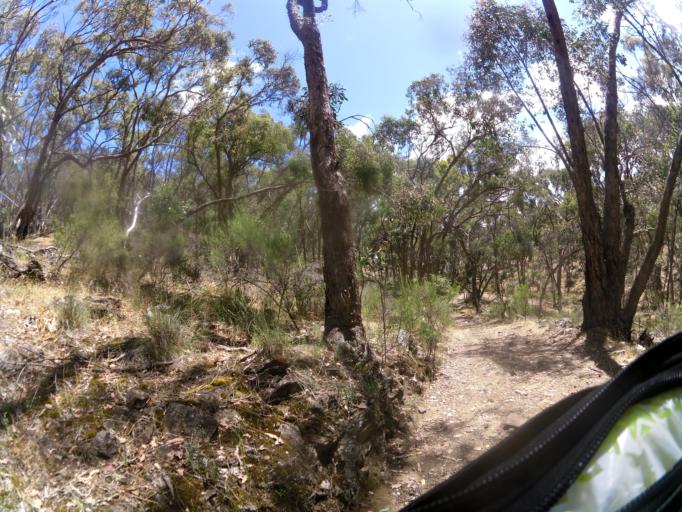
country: AU
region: Victoria
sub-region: Mount Alexander
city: Castlemaine
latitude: -37.0637
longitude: 144.2663
